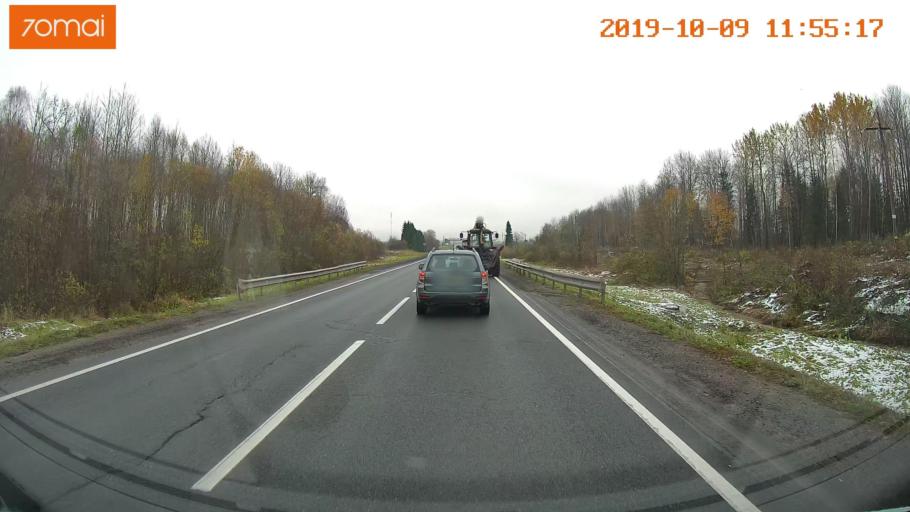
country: RU
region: Vologda
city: Gryazovets
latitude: 58.7503
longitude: 40.2850
